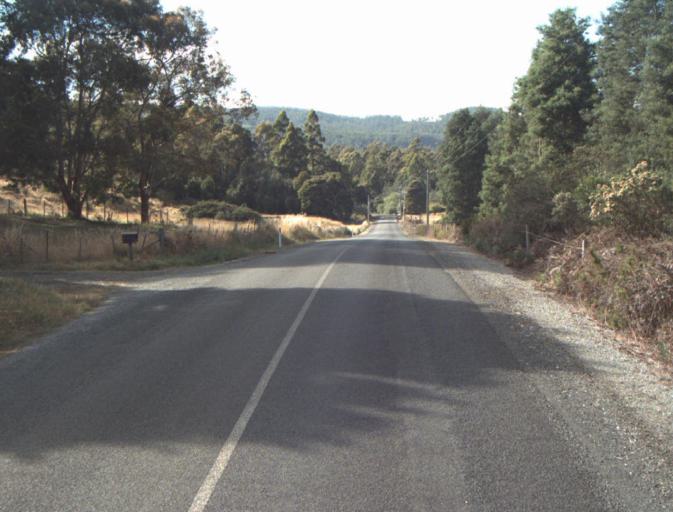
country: AU
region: Tasmania
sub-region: Launceston
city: Mayfield
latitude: -41.2816
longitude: 147.1950
